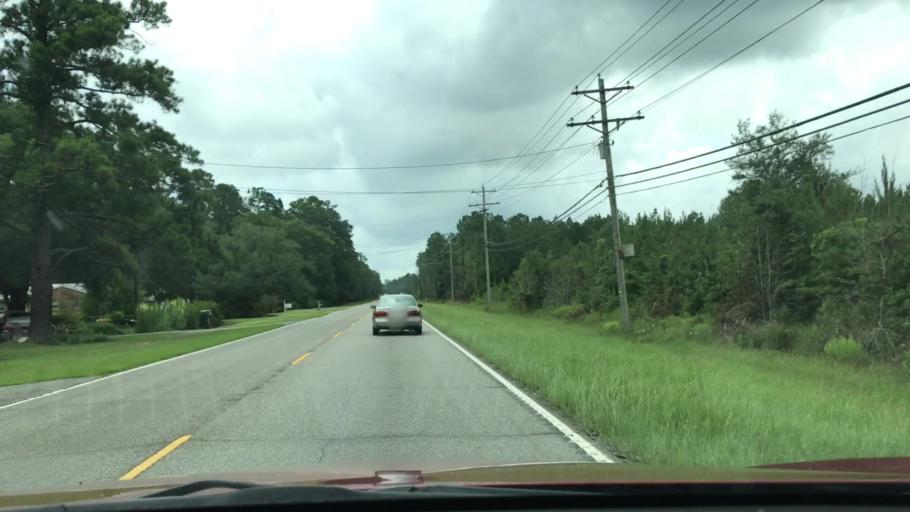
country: US
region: South Carolina
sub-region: Georgetown County
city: Georgetown
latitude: 33.4263
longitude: -79.2804
